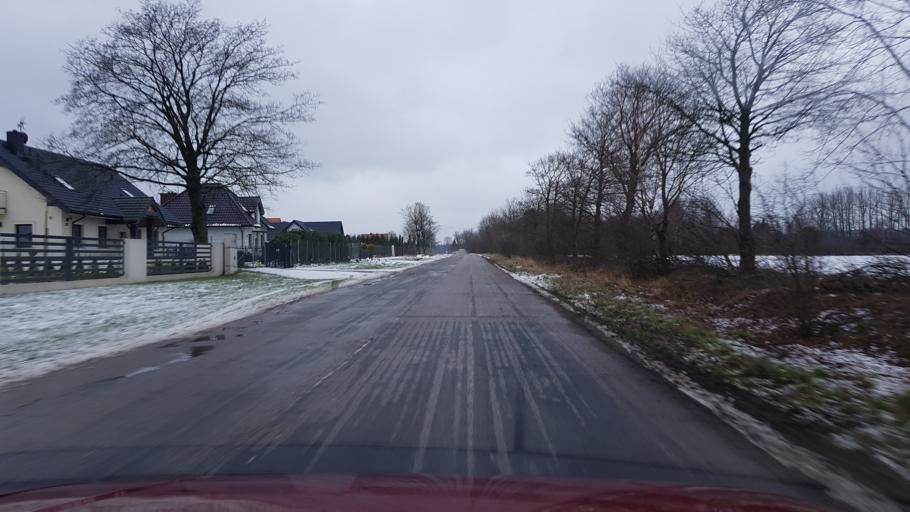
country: PL
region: West Pomeranian Voivodeship
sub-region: Powiat goleniowski
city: Nowogard
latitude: 53.6521
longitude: 15.1239
